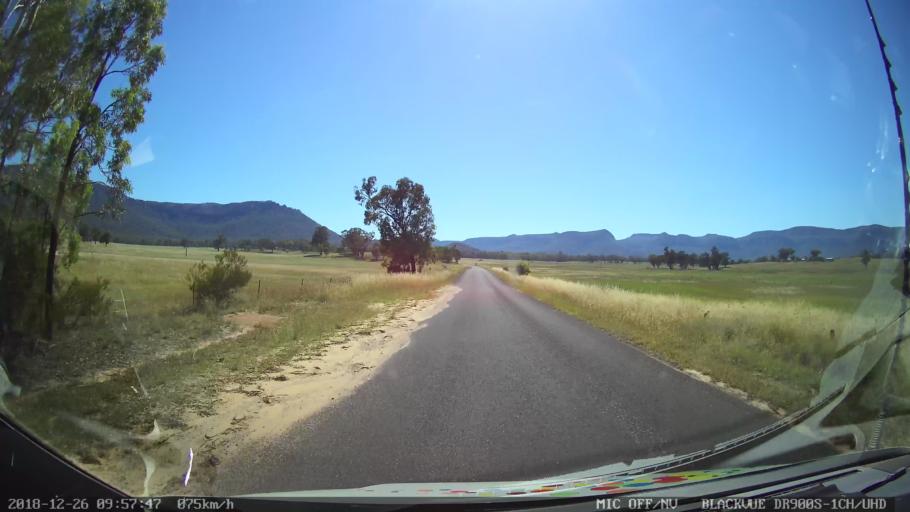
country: AU
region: New South Wales
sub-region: Mid-Western Regional
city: Kandos
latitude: -33.0406
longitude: 150.1966
